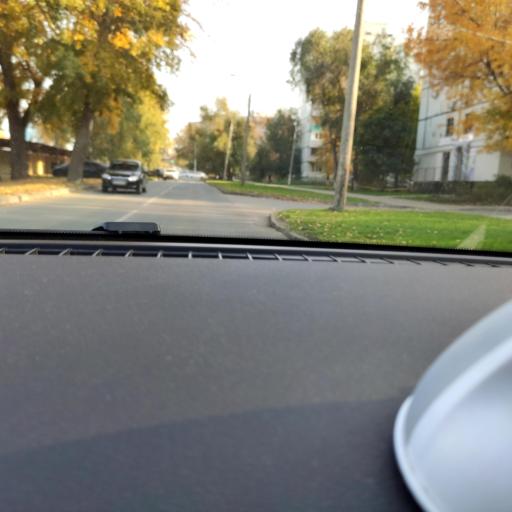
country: RU
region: Samara
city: Samara
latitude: 53.2081
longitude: 50.1436
